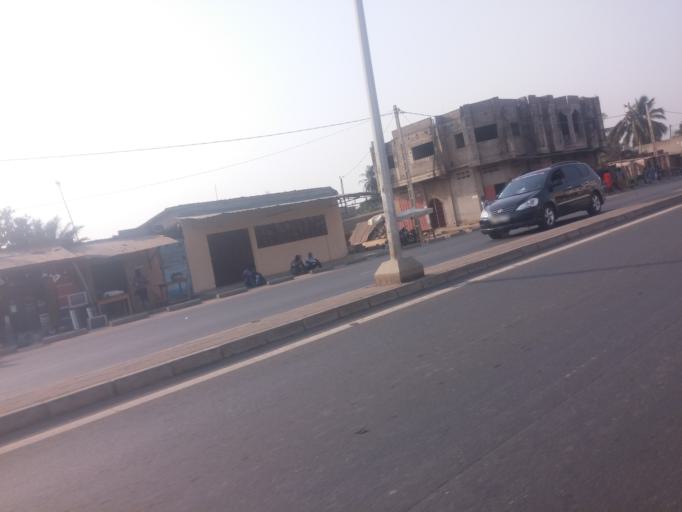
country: TG
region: Maritime
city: Lome
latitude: 6.1689
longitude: 1.2826
